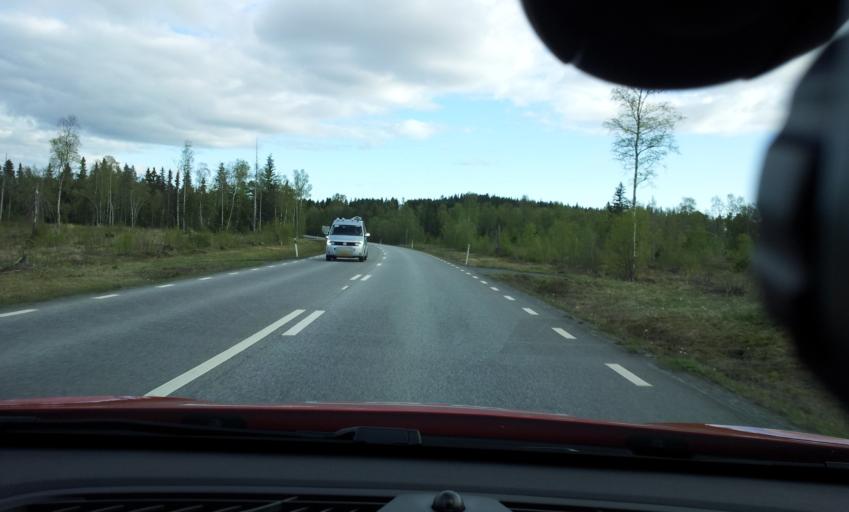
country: SE
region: Jaemtland
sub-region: OEstersunds Kommun
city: Ostersund
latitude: 63.1805
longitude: 14.5342
